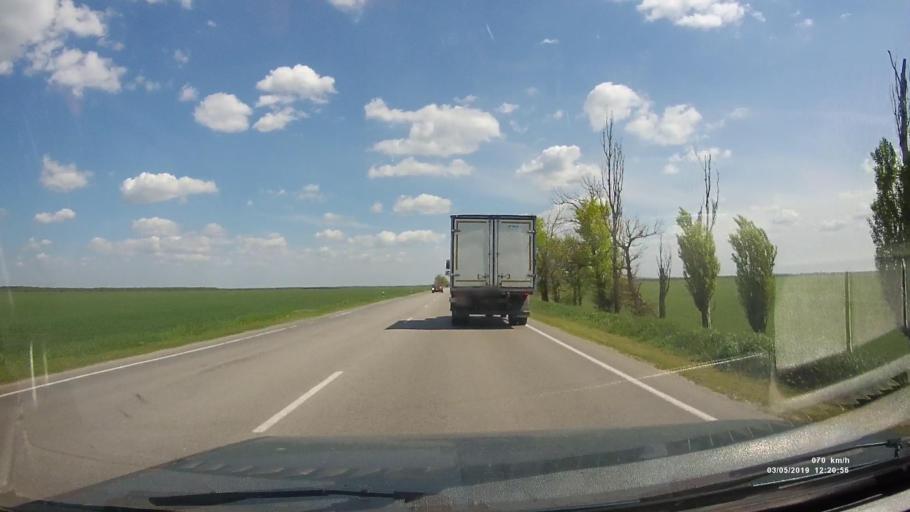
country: RU
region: Rostov
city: Melikhovskaya
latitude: 47.4049
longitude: 40.6298
